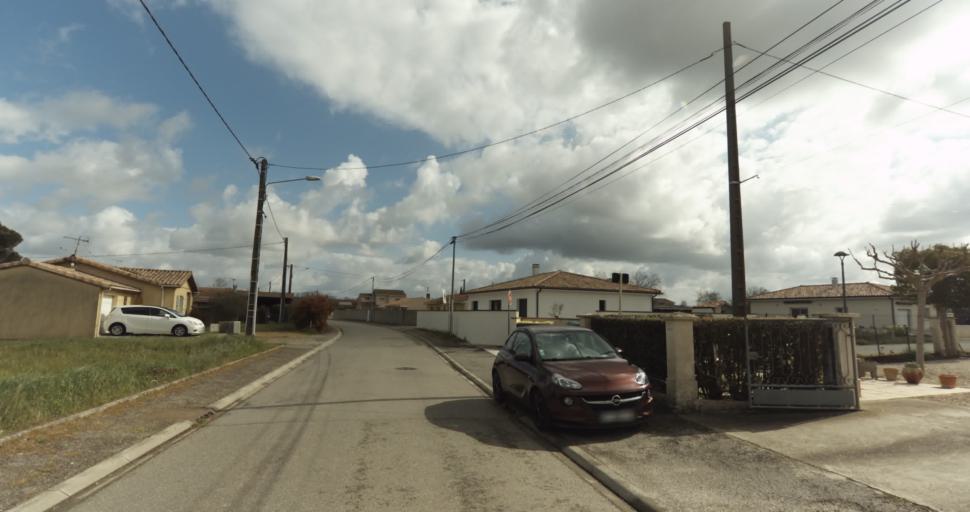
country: FR
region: Midi-Pyrenees
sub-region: Departement de la Haute-Garonne
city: Auterive
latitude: 43.3463
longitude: 1.4610
